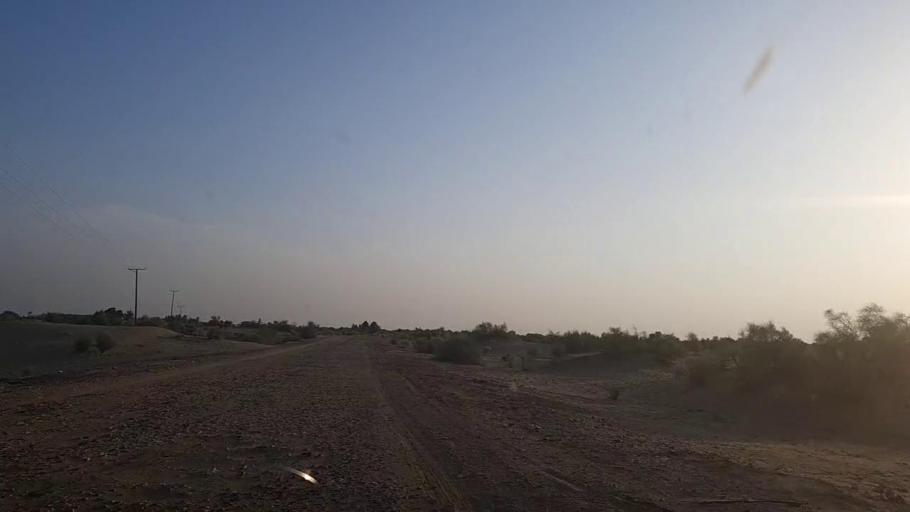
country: PK
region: Sindh
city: Khanpur
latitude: 27.6415
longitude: 69.4551
